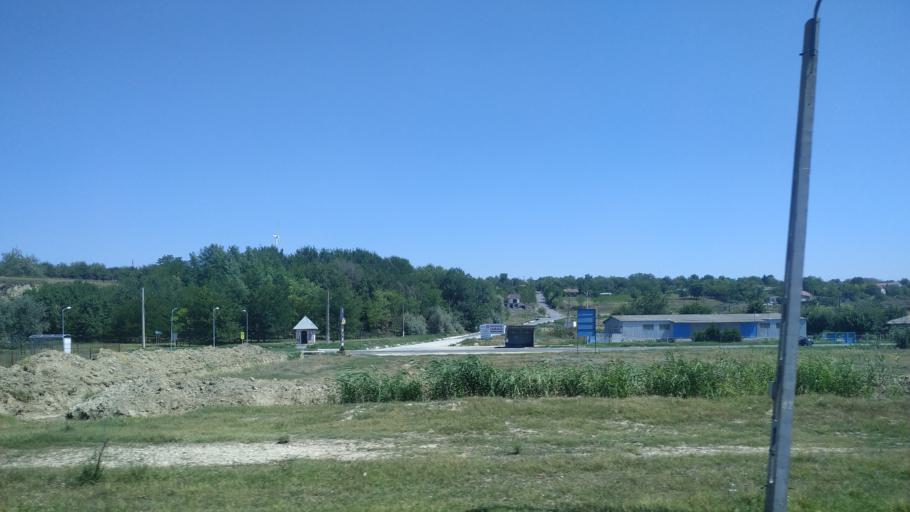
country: RO
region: Constanta
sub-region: Comuna Saligny
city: Saligny
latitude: 44.2838
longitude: 28.0802
